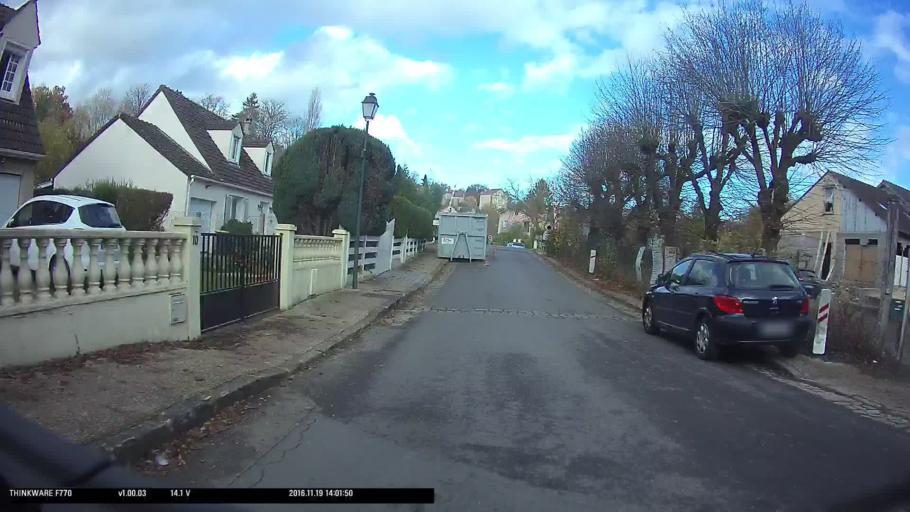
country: FR
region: Ile-de-France
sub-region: Departement du Val-d'Oise
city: Ableiges
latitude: 49.0804
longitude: 2.0033
